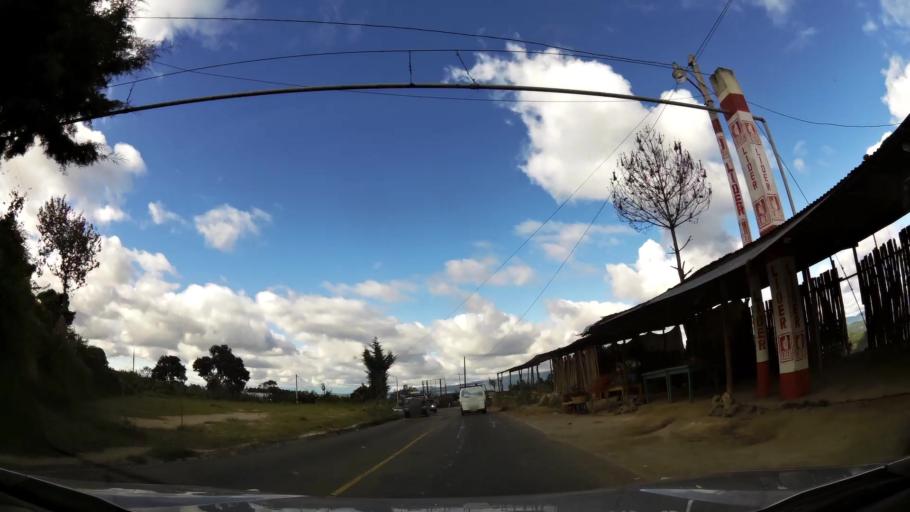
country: GT
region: Quiche
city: Chichicastenango
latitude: 14.9242
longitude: -91.1062
